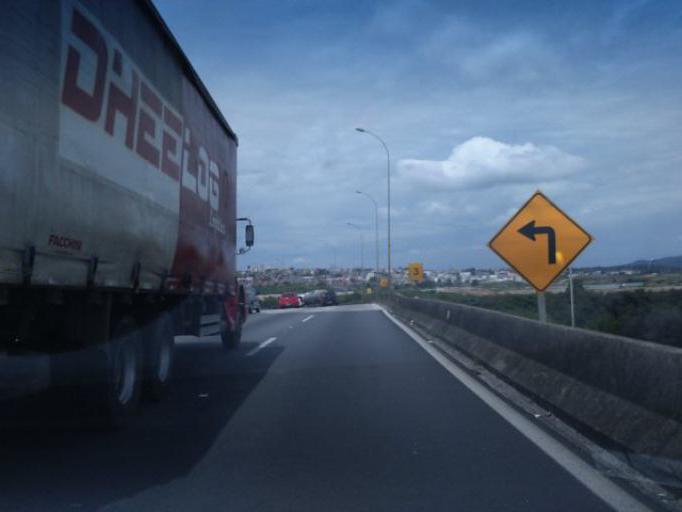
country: BR
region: Sao Paulo
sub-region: Carapicuiba
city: Carapicuiba
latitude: -23.5180
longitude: -46.8150
